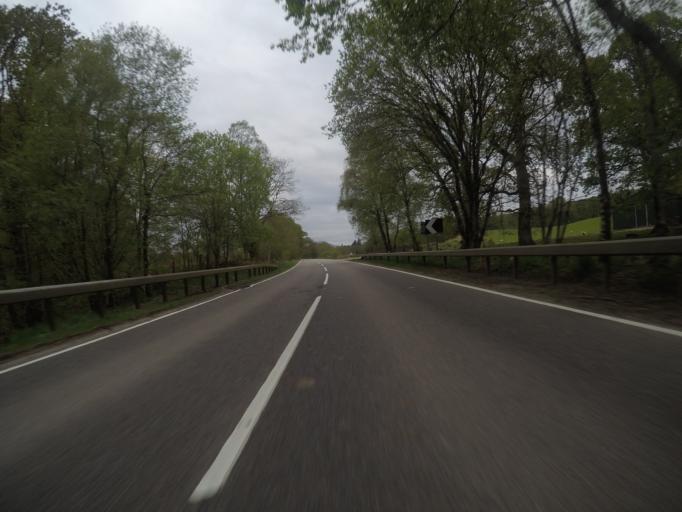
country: GB
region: Scotland
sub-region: Highland
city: Spean Bridge
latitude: 56.8949
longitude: -4.8962
